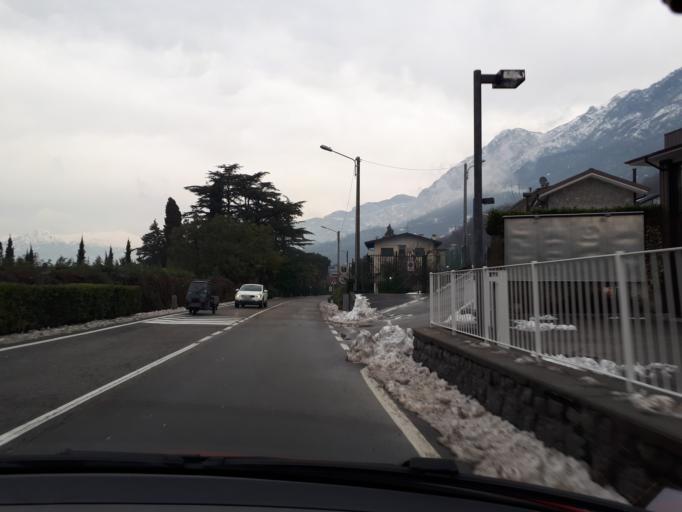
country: IT
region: Lombardy
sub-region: Provincia di Lecco
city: Mandello del Lario
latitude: 45.9263
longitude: 9.3120
